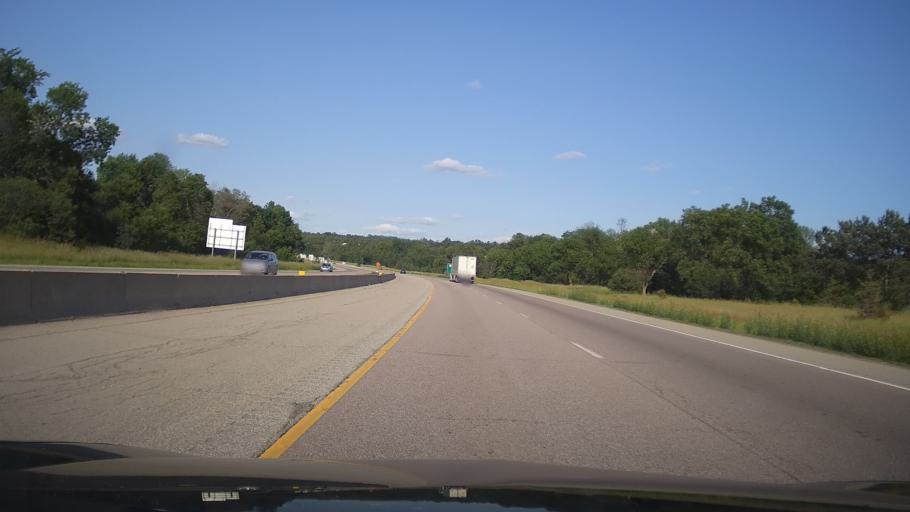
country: CA
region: Ontario
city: Skatepark
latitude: 44.2653
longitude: -76.9426
